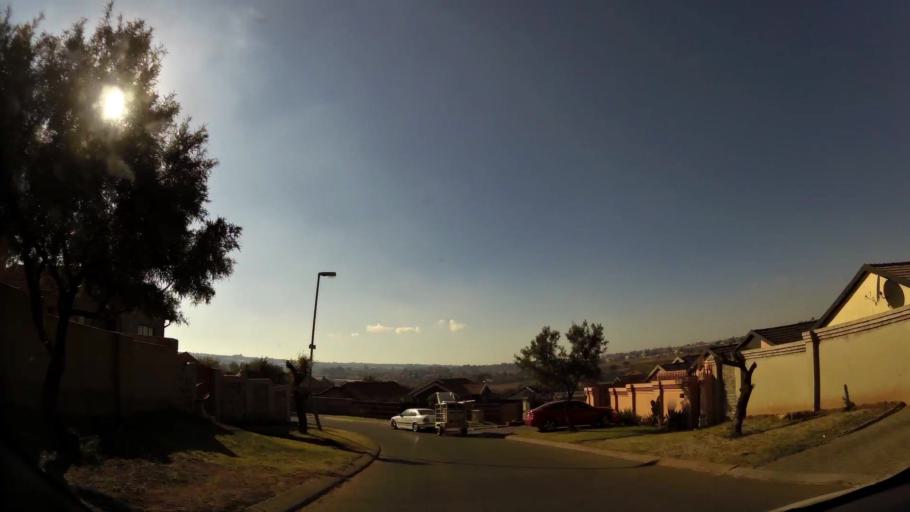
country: ZA
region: Gauteng
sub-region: City of Johannesburg Metropolitan Municipality
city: Roodepoort
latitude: -26.1560
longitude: 27.8353
